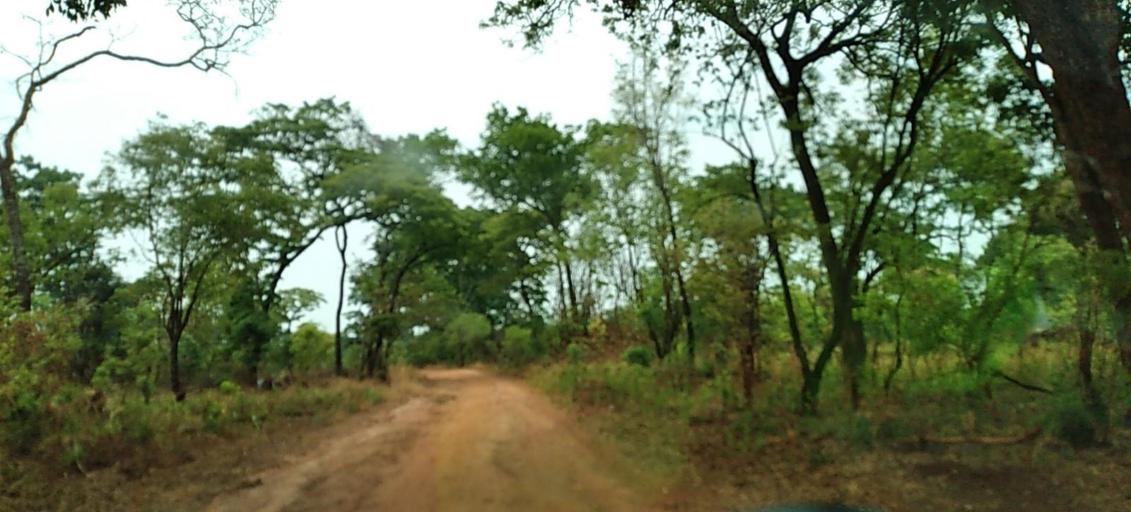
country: ZM
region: North-Western
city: Solwezi
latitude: -12.3284
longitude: 26.5204
